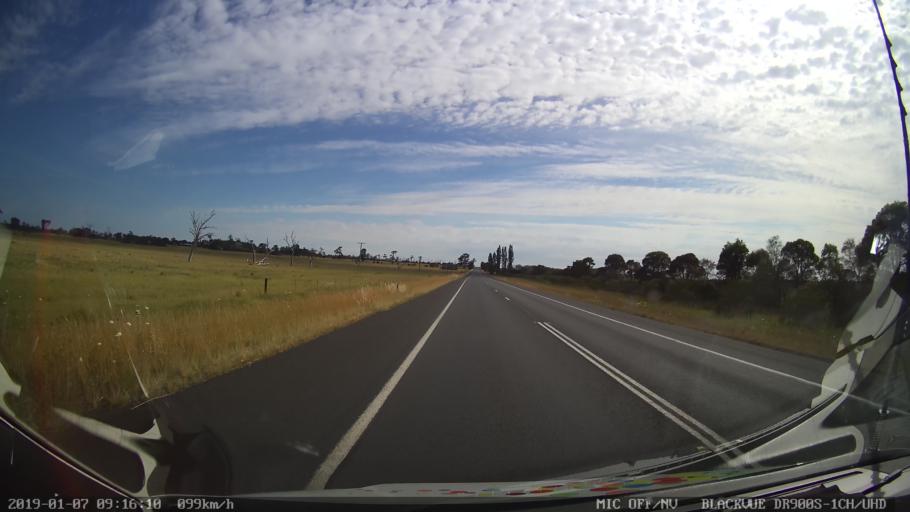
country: AU
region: New South Wales
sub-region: Armidale Dumaresq
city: Armidale
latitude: -30.6054
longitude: 151.5422
